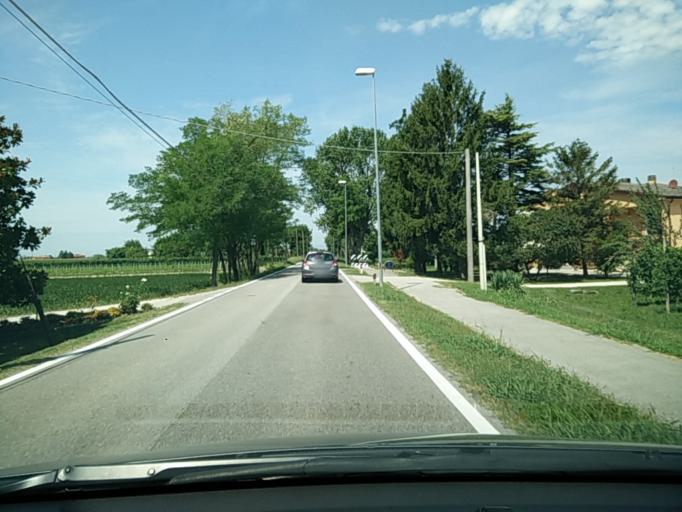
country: IT
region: Veneto
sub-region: Provincia di Venezia
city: Passarella
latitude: 45.5727
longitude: 12.6188
